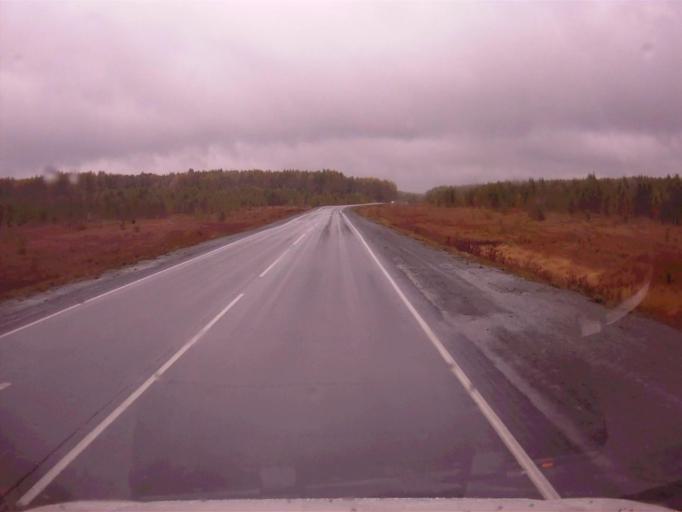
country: RU
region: Chelyabinsk
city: Tayginka
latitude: 55.5049
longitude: 60.6367
